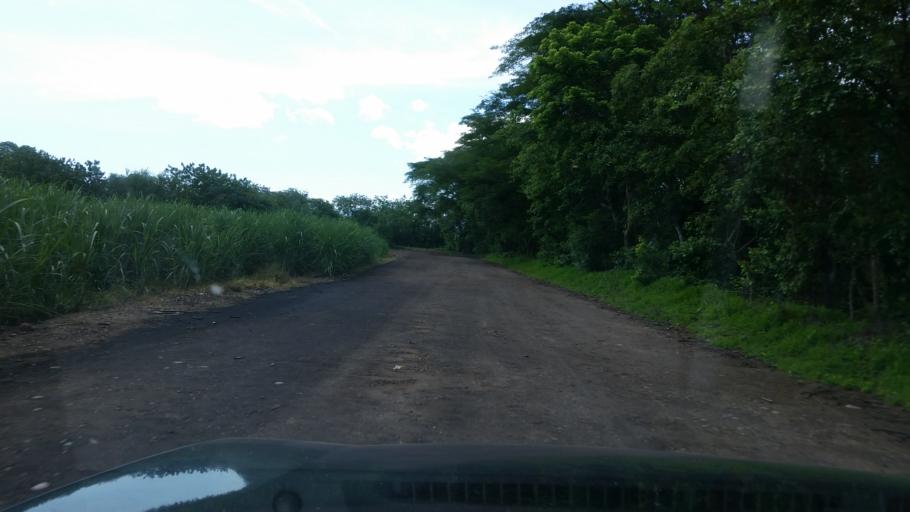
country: NI
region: Chinandega
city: El Viejo
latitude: 12.7458
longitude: -87.1354
